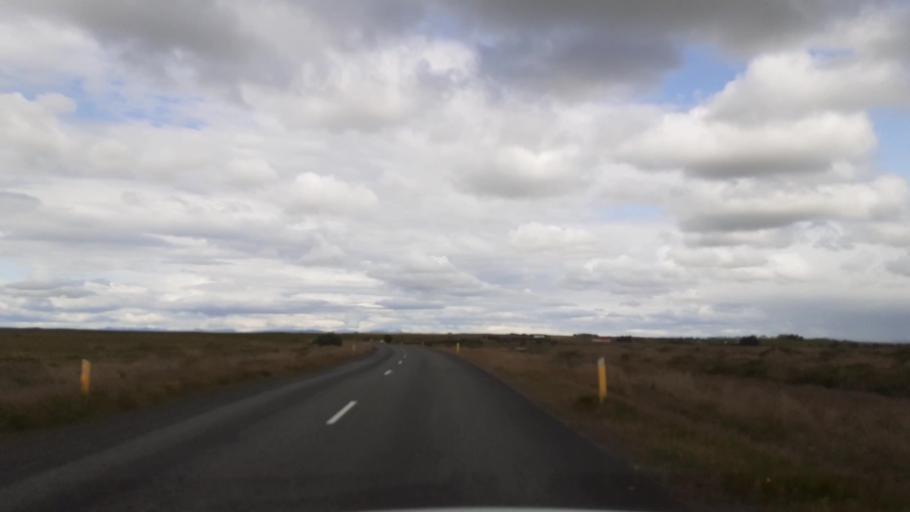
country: IS
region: South
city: Vestmannaeyjar
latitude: 63.8219
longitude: -20.4273
